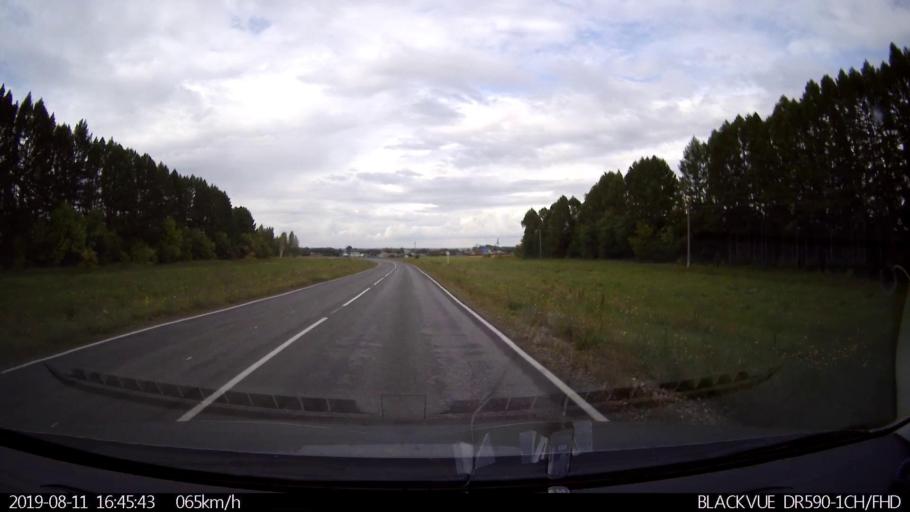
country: RU
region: Ulyanovsk
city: Mayna
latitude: 54.1925
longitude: 47.6877
